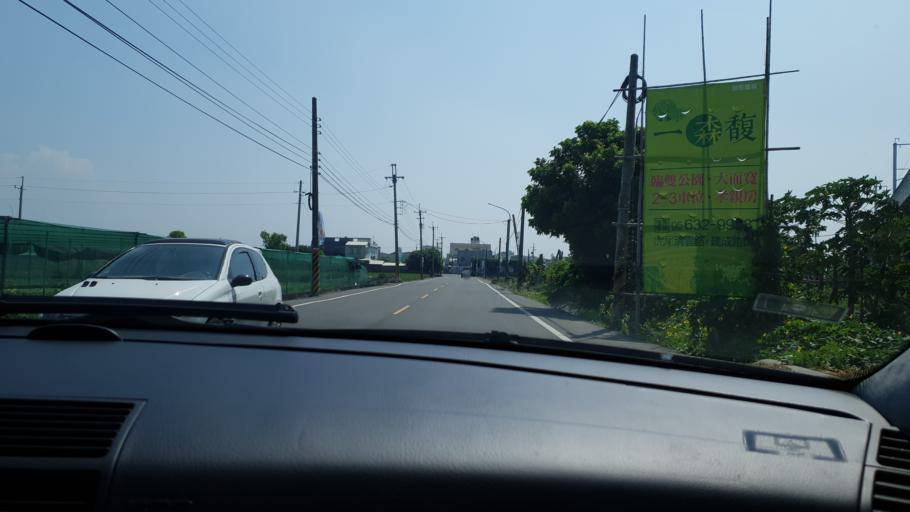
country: TW
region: Taiwan
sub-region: Yunlin
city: Douliu
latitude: 23.7505
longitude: 120.4217
